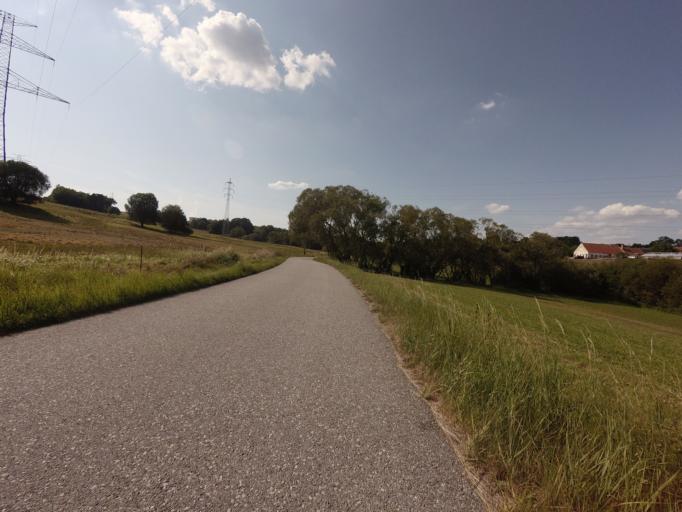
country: CZ
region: Jihocesky
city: Tyn nad Vltavou
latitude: 49.1711
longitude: 14.4225
